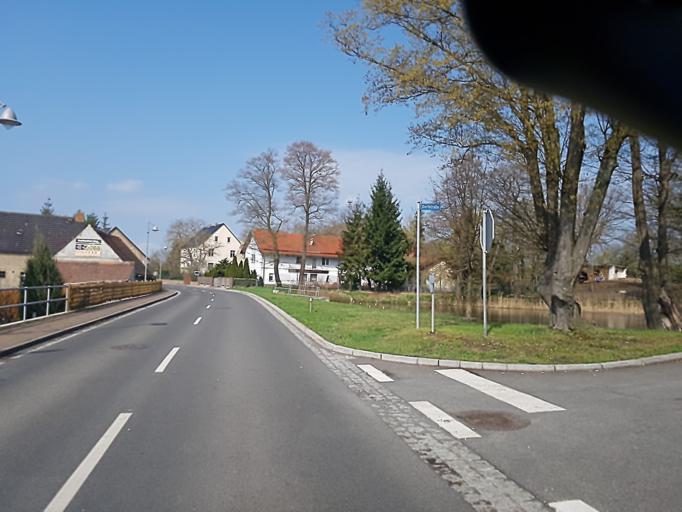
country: DE
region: Saxony
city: Elsnig
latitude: 51.5625
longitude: 12.8807
